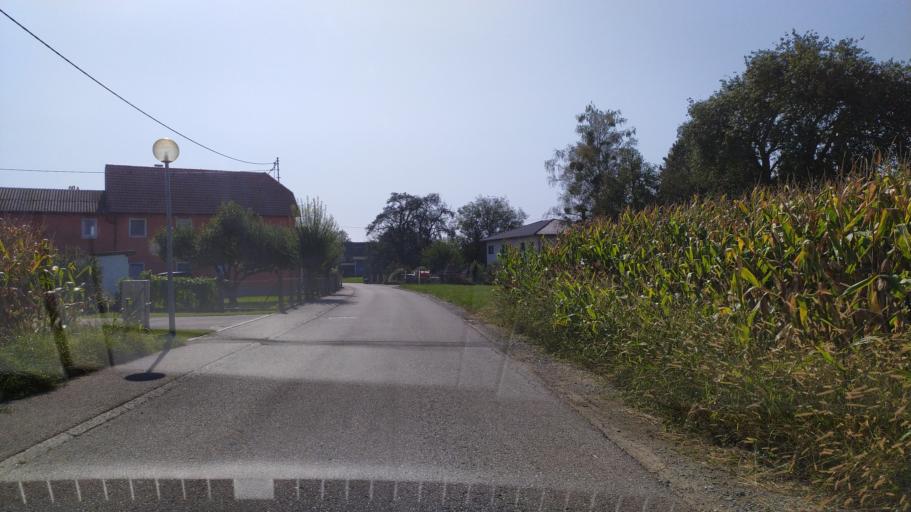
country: AT
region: Lower Austria
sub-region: Politischer Bezirk Amstetten
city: Strengberg
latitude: 48.1875
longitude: 14.7078
